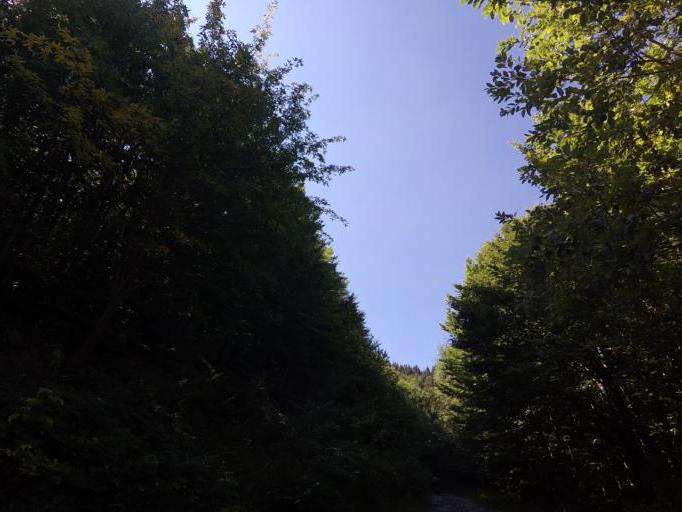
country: IT
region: Emilia-Romagna
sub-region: Provincia di Modena
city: Montecreto
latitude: 44.2268
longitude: 10.7249
